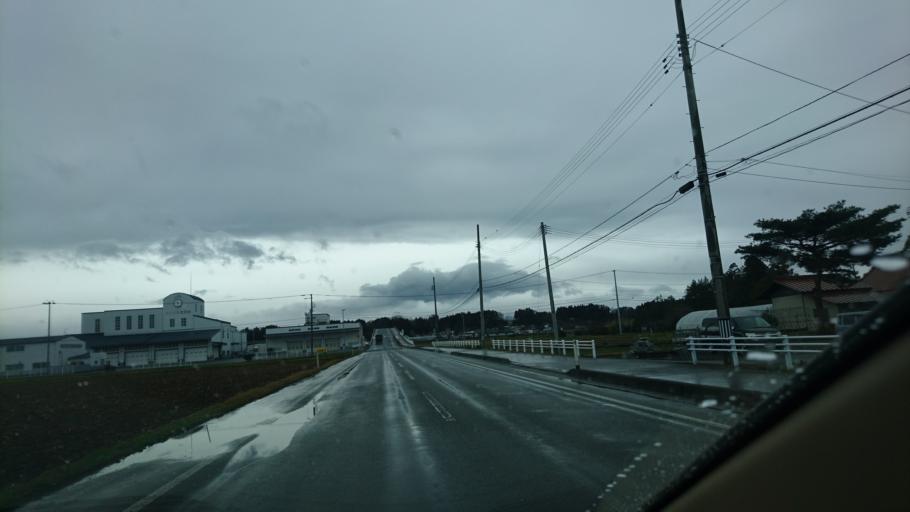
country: JP
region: Iwate
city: Mizusawa
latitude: 39.0982
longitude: 141.1474
